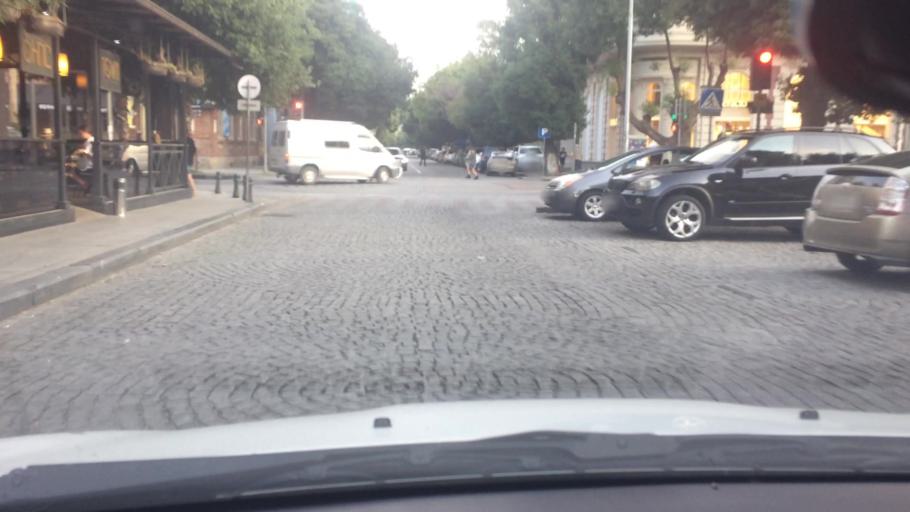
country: GE
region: Ajaria
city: Batumi
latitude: 41.6518
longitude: 41.6336
